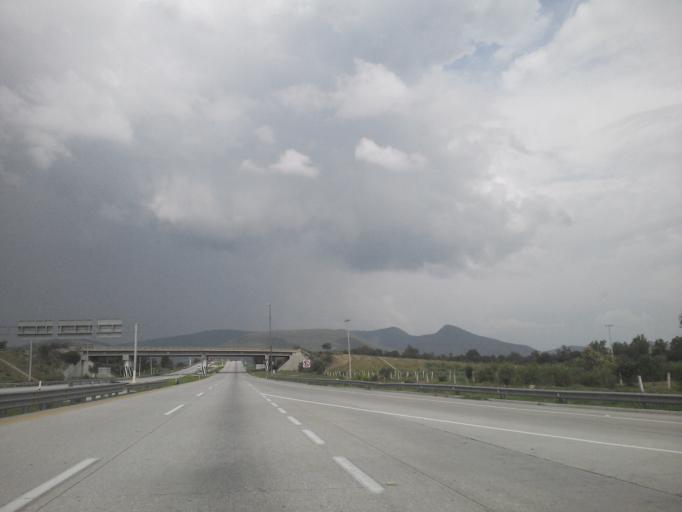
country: MX
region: Hidalgo
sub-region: Atitalaquia
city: Atitalaquia
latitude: 20.0654
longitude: -99.2160
